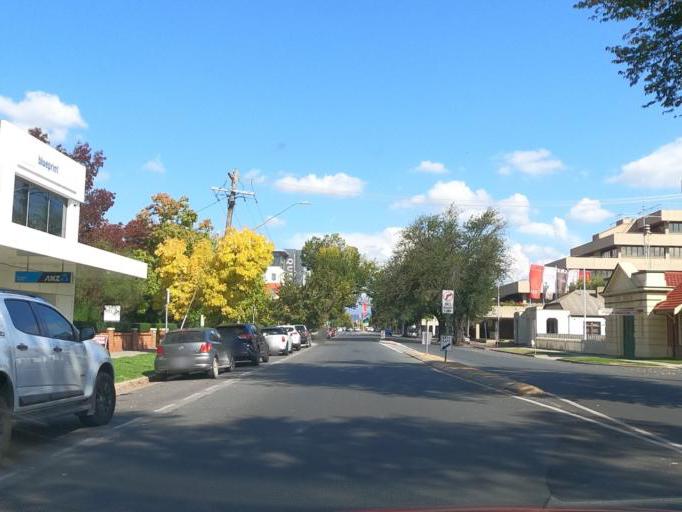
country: AU
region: New South Wales
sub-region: Albury Municipality
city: Albury
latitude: -36.0767
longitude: 146.9164
